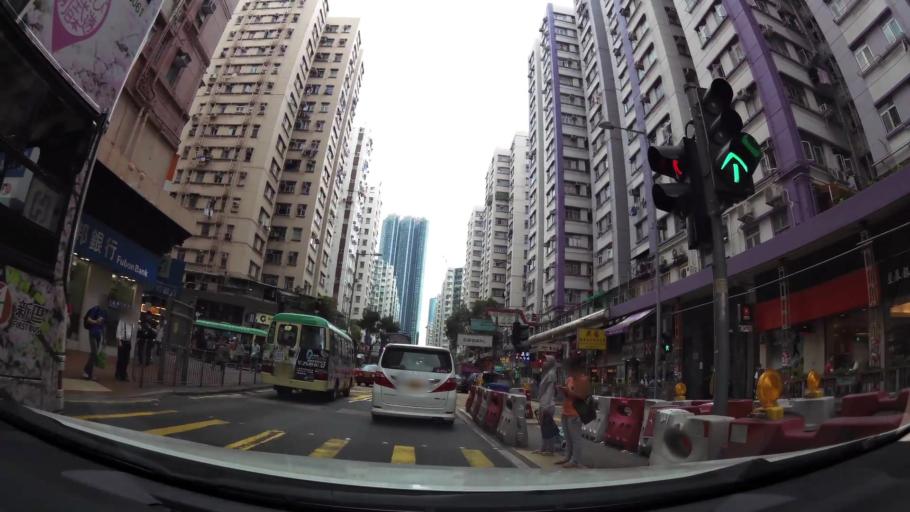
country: HK
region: Kowloon City
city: Kowloon
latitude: 22.3063
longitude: 114.1875
